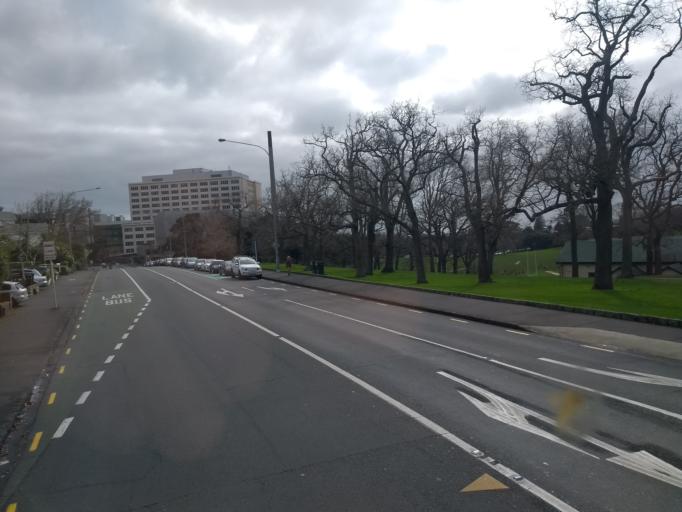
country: NZ
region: Auckland
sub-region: Auckland
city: Auckland
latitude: -36.8639
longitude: 174.7711
